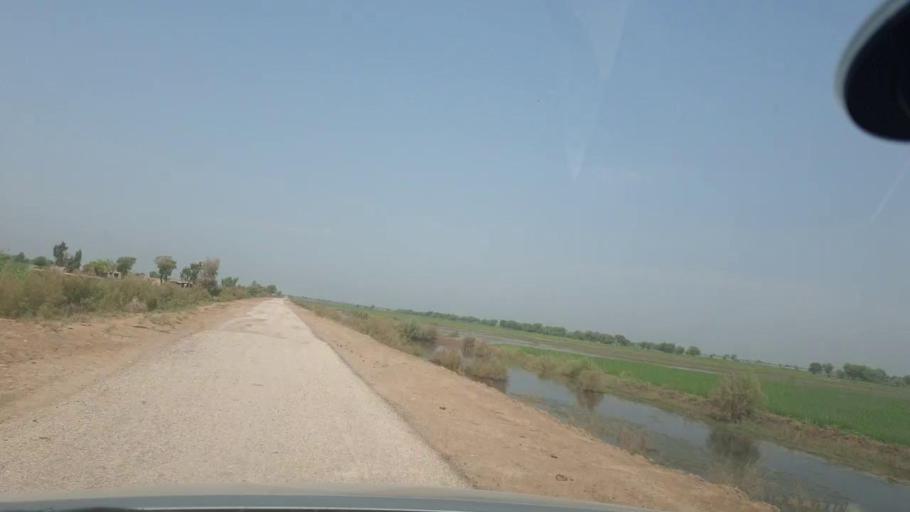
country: PK
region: Balochistan
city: Mehrabpur
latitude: 28.0641
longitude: 68.0637
